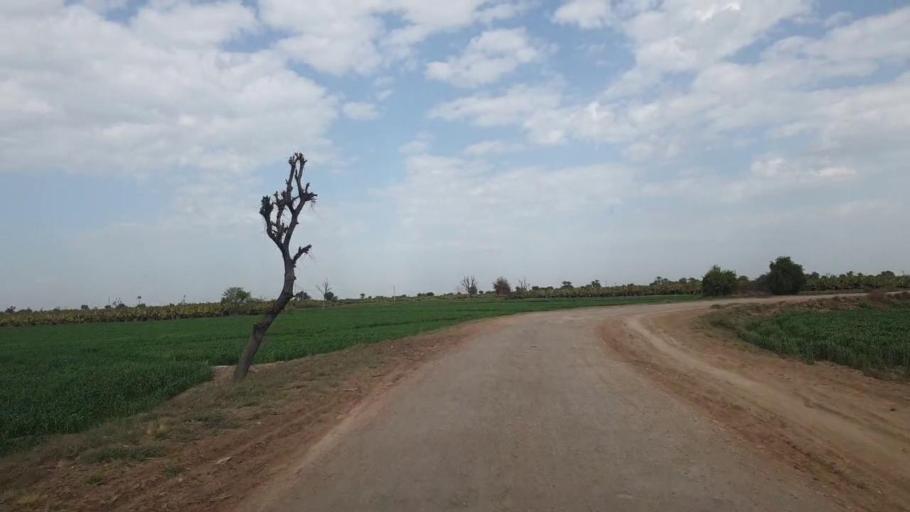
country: PK
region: Sindh
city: Shahdadpur
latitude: 25.9650
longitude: 68.4705
